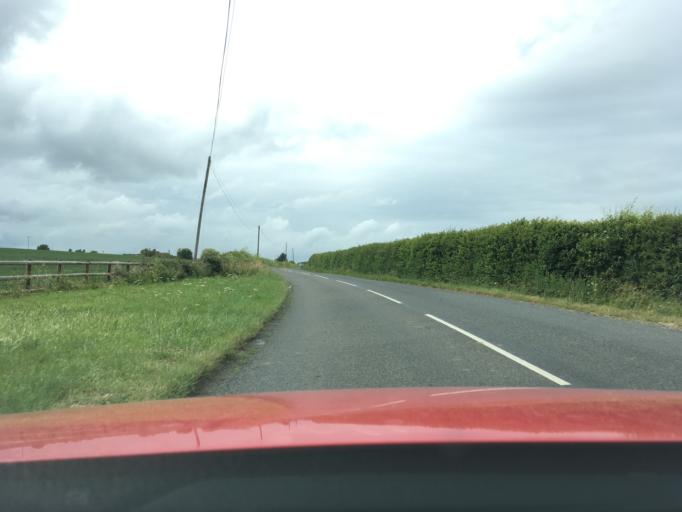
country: GB
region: England
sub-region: Worcestershire
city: Badsey
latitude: 52.0522
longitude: -1.9202
